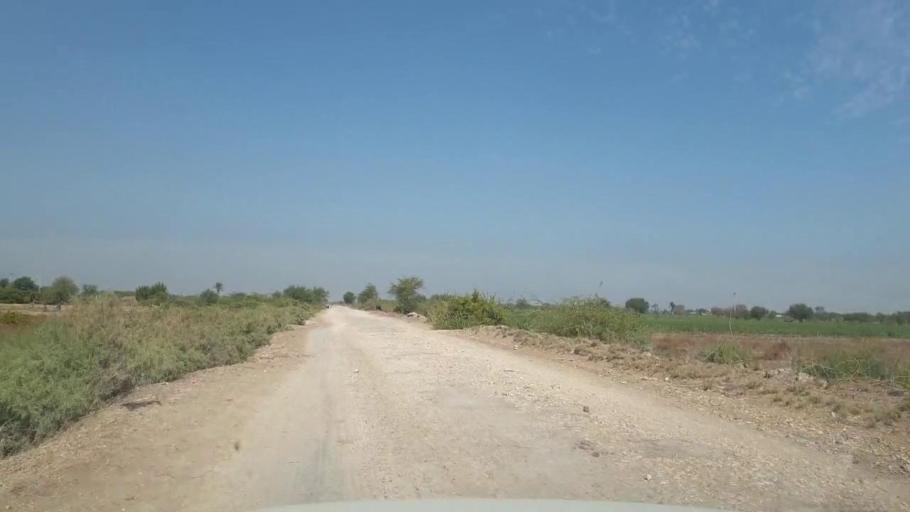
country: PK
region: Sindh
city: Mirpur Khas
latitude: 25.5935
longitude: 69.2010
